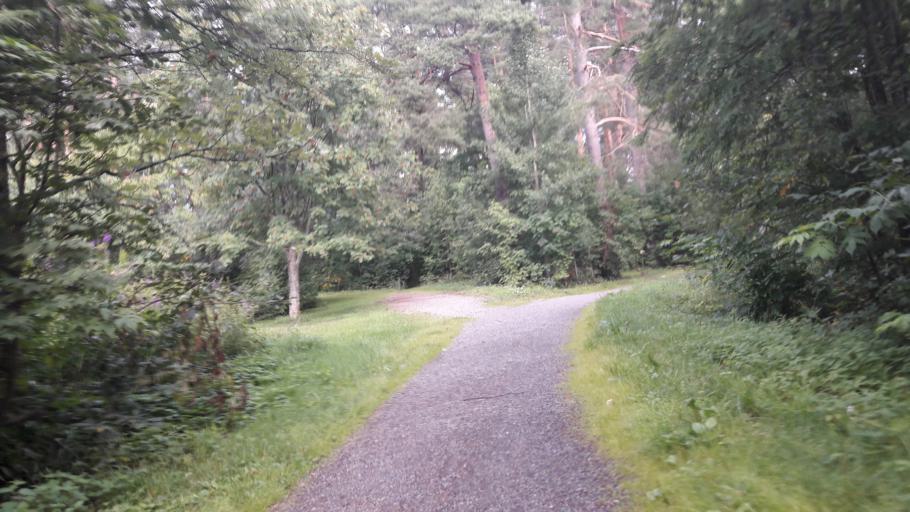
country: FI
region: North Karelia
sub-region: Joensuu
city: Joensuu
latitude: 62.5771
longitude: 29.8045
